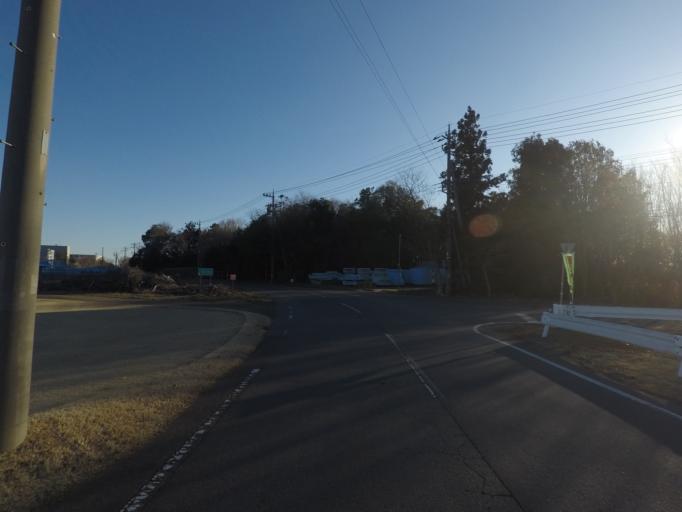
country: JP
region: Ibaraki
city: Ishige
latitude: 36.1191
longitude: 140.0263
